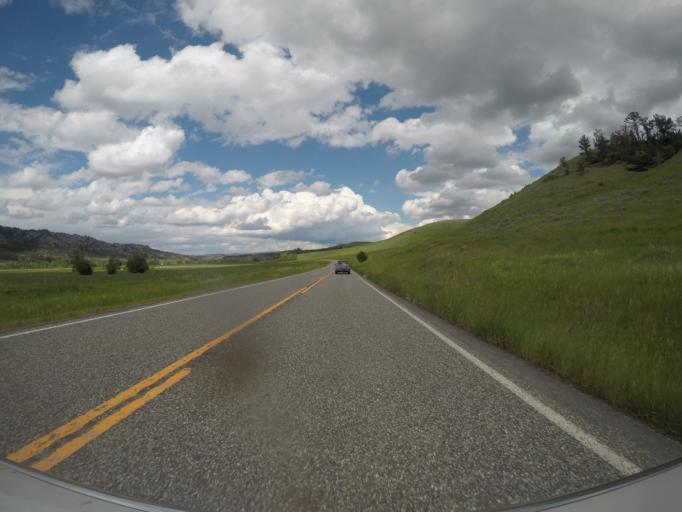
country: US
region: Montana
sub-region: Sweet Grass County
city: Big Timber
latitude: 45.6916
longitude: -110.0426
